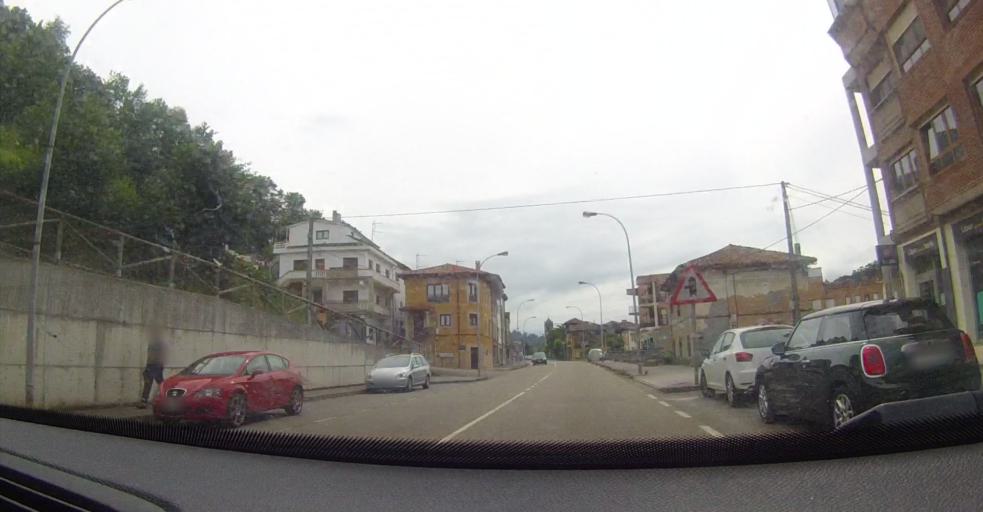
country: ES
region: Asturias
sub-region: Province of Asturias
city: Pilona
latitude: 43.3608
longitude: -5.3037
